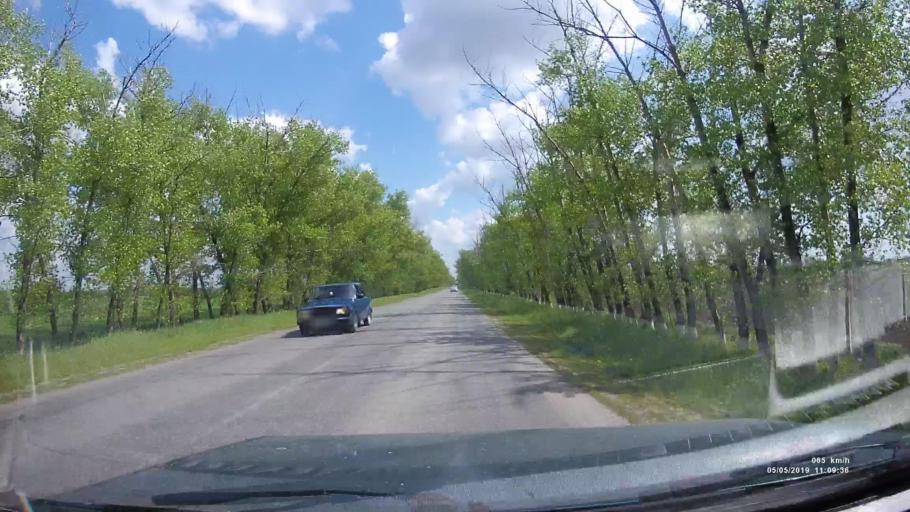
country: RU
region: Rostov
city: Ust'-Donetskiy
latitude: 47.7412
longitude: 40.9269
